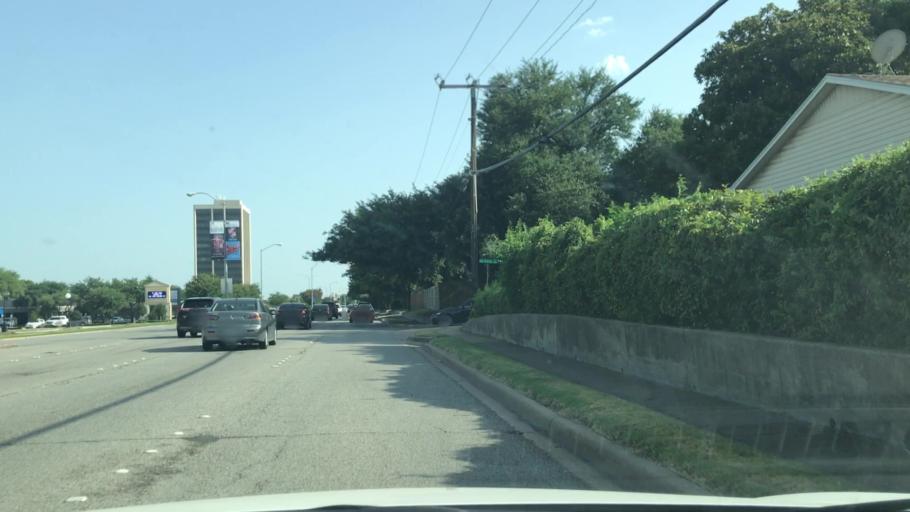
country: US
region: Texas
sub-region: Dallas County
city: Richardson
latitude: 32.9599
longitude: -96.7690
